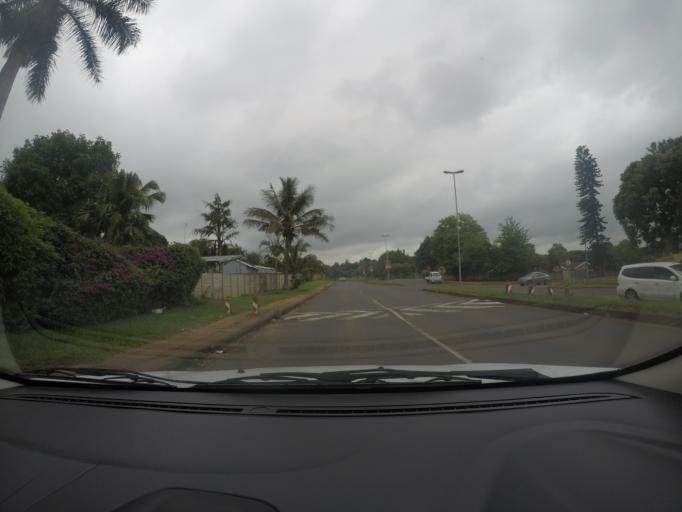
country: ZA
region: KwaZulu-Natal
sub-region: uThungulu District Municipality
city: Empangeni
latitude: -28.7603
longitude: 31.8971
